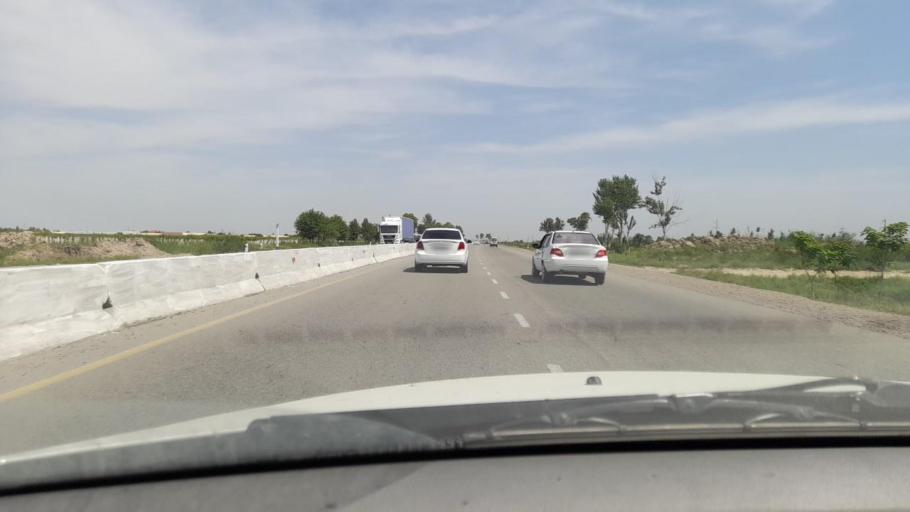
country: UZ
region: Bukhara
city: Galaosiyo
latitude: 39.8921
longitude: 64.4673
